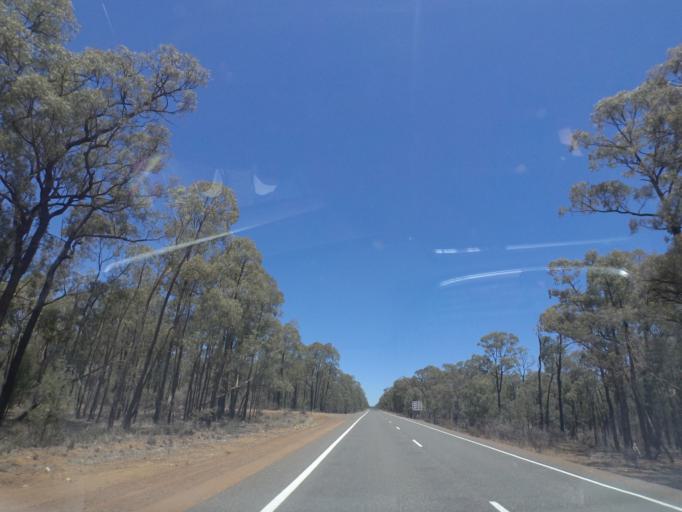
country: AU
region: New South Wales
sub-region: Warrumbungle Shire
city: Coonabarabran
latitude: -30.8578
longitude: 149.4554
